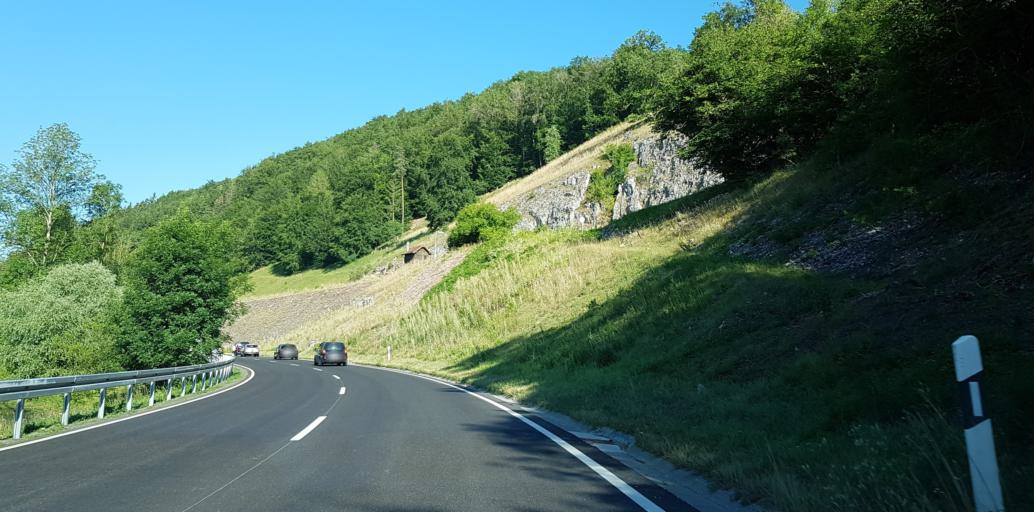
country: DE
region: Baden-Wuerttemberg
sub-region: Tuebingen Region
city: Blaubeuren
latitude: 48.4020
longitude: 9.8256
